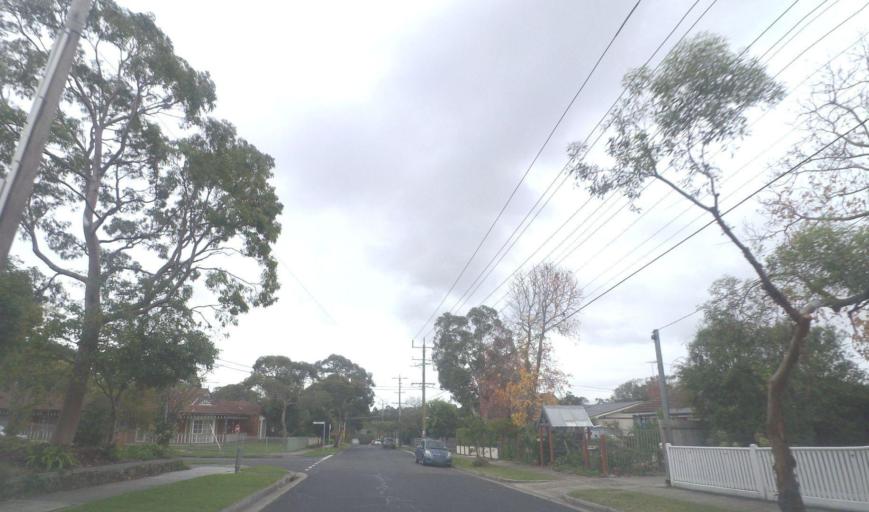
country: AU
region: Victoria
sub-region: Whitehorse
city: Blackburn North
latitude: -37.8030
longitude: 145.1534
